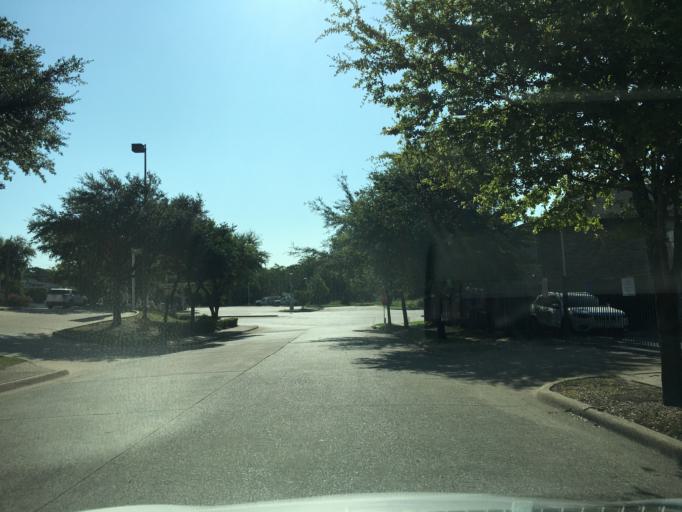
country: US
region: Texas
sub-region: Dallas County
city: Garland
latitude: 32.8635
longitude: -96.7013
